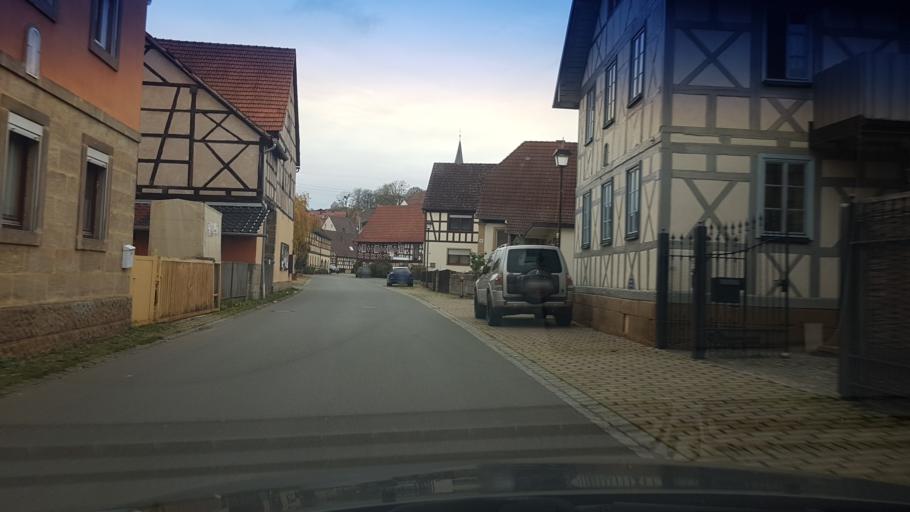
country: DE
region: Bavaria
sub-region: Upper Franconia
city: Rattelsdorf
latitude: 50.0612
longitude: 10.8656
